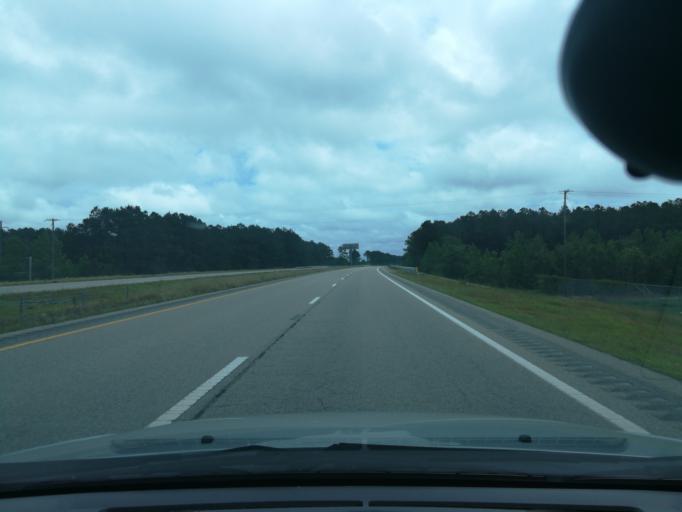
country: US
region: North Carolina
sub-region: Chowan County
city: Edenton
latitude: 35.9074
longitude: -76.4768
